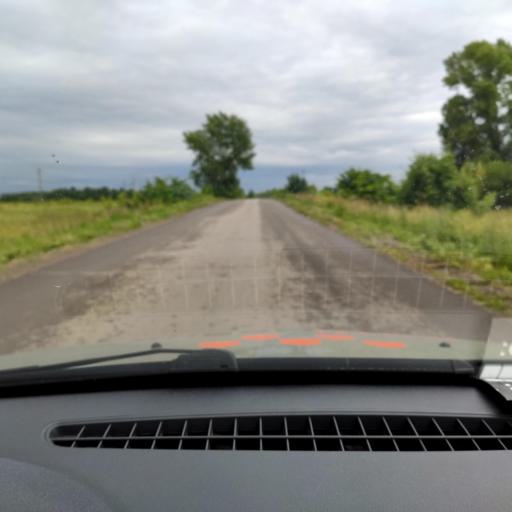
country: RU
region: Bashkortostan
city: Iglino
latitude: 54.8965
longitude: 56.2754
